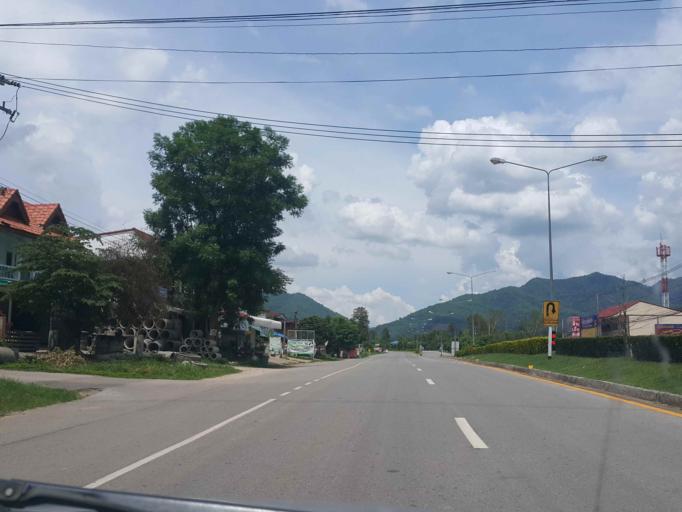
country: TH
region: Nan
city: Ban Luang
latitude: 18.8499
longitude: 100.4395
